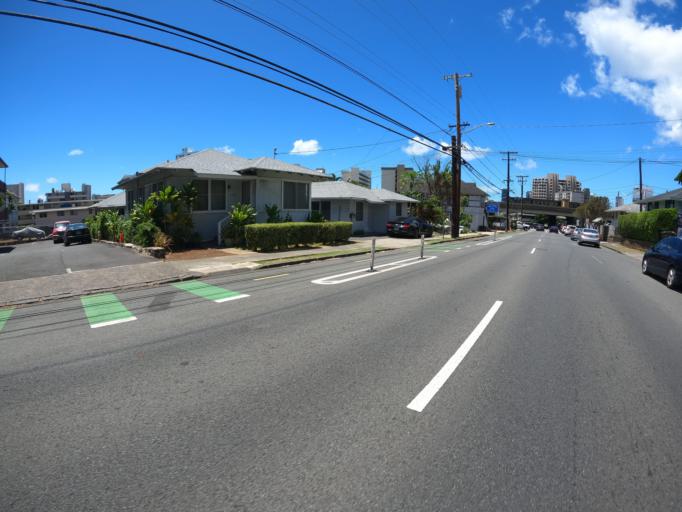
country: US
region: Hawaii
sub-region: Honolulu County
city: Honolulu
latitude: 21.3050
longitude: -157.8436
